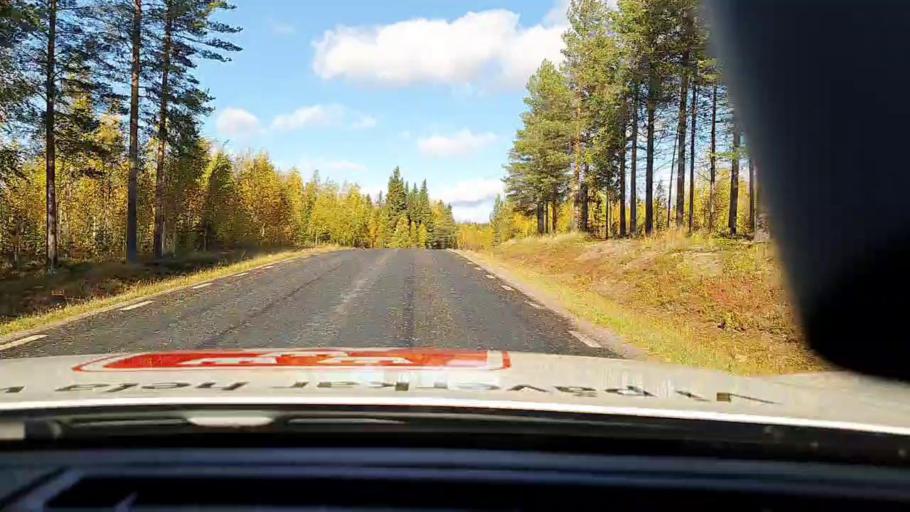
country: SE
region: Vaesterbotten
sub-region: Skelleftea Kommun
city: Langsele
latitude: 65.0172
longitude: 20.0768
